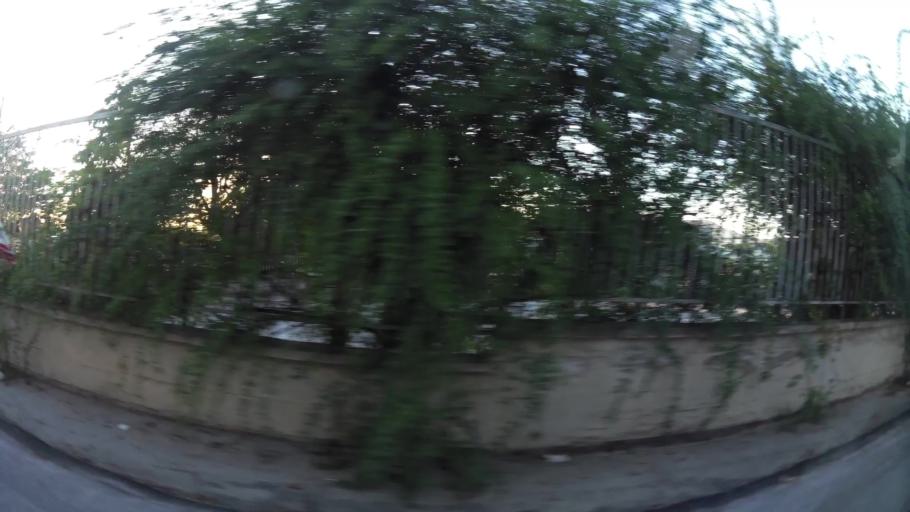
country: GR
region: Attica
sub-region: Nomarchia Anatolikis Attikis
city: Kryoneri
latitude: 38.1284
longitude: 23.8351
